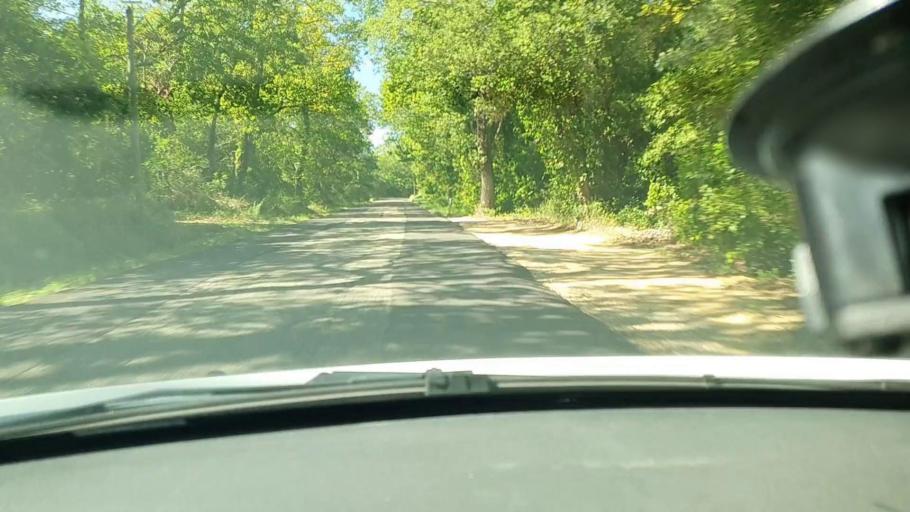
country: FR
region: Languedoc-Roussillon
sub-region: Departement du Gard
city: Sabran
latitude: 44.1748
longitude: 4.5081
